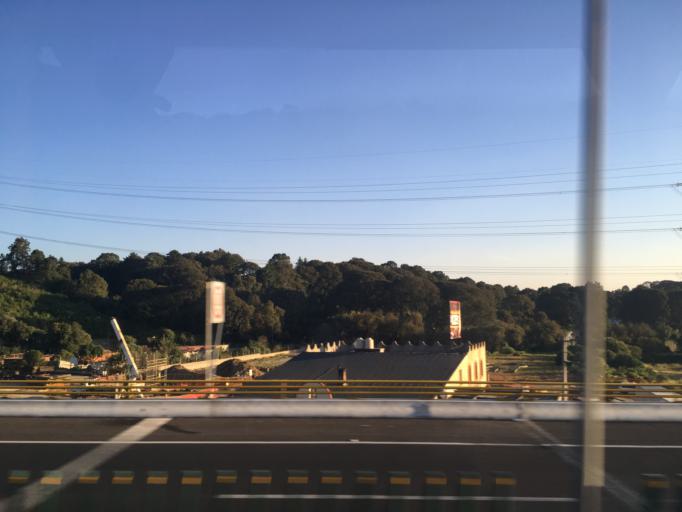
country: MX
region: Mexico
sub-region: Lerma
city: San Miguel Ameyalco
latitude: 19.2896
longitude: -99.4370
